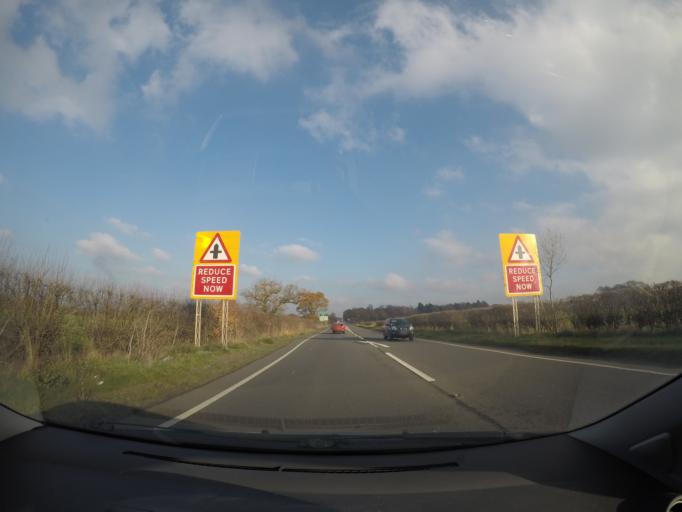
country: GB
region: England
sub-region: City of York
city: Holtby
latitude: 54.0108
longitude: -0.9949
